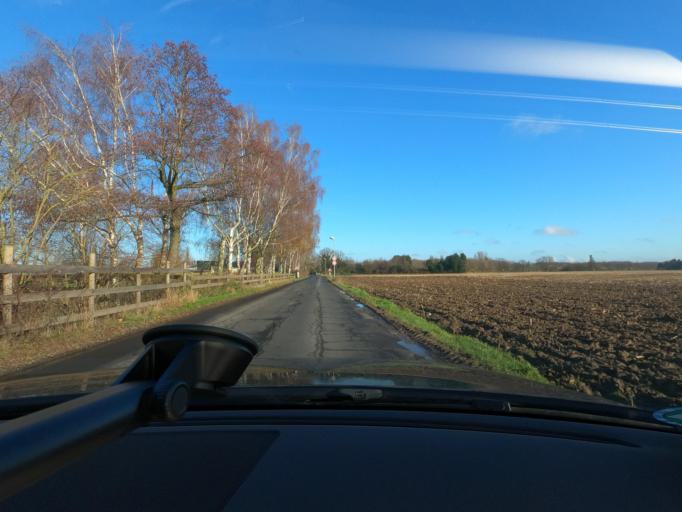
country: DE
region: North Rhine-Westphalia
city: Tonisvorst
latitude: 51.3339
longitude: 6.5152
